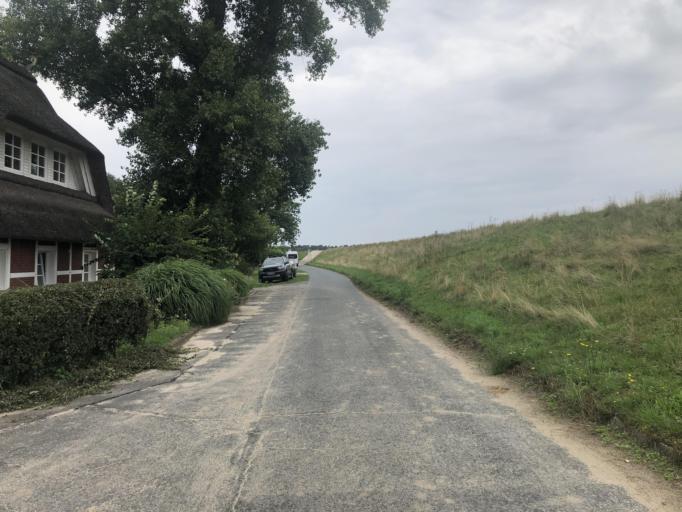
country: DE
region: Mecklenburg-Vorpommern
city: Nostorf
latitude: 53.3655
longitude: 10.6485
